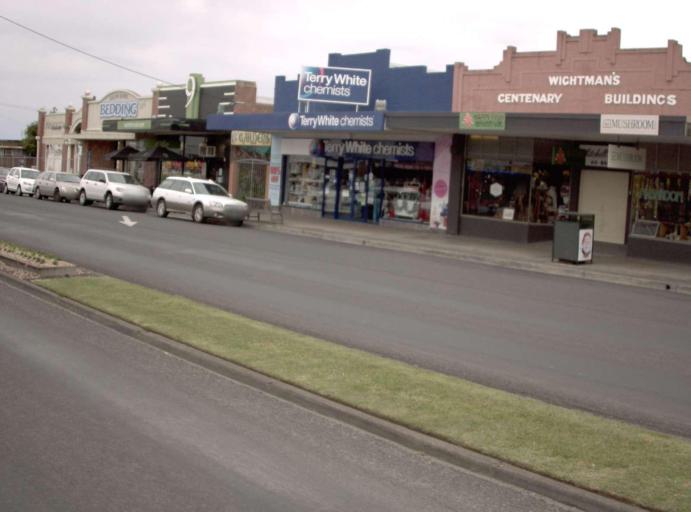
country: AU
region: Victoria
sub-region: Baw Baw
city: Warragul
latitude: -38.4777
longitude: 145.9469
